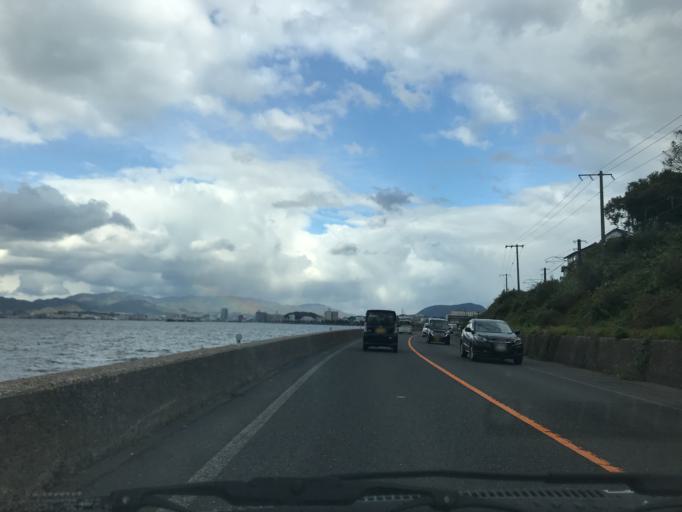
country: JP
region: Shimane
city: Matsue-shi
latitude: 35.4396
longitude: 133.0387
